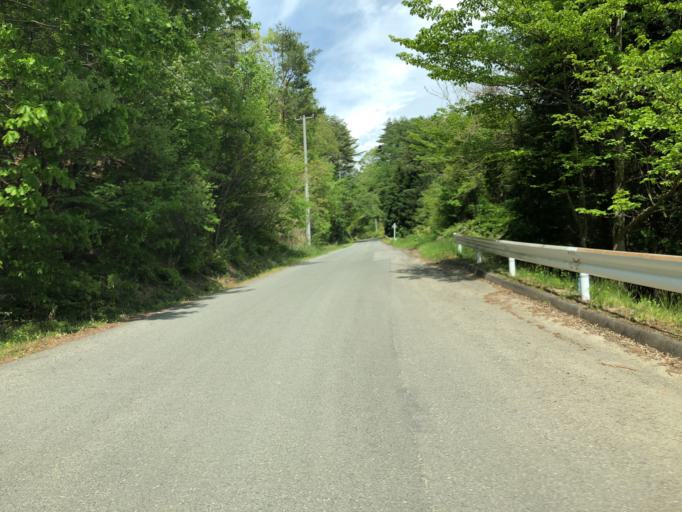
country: JP
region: Fukushima
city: Yanagawamachi-saiwaicho
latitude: 37.7417
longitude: 140.7072
